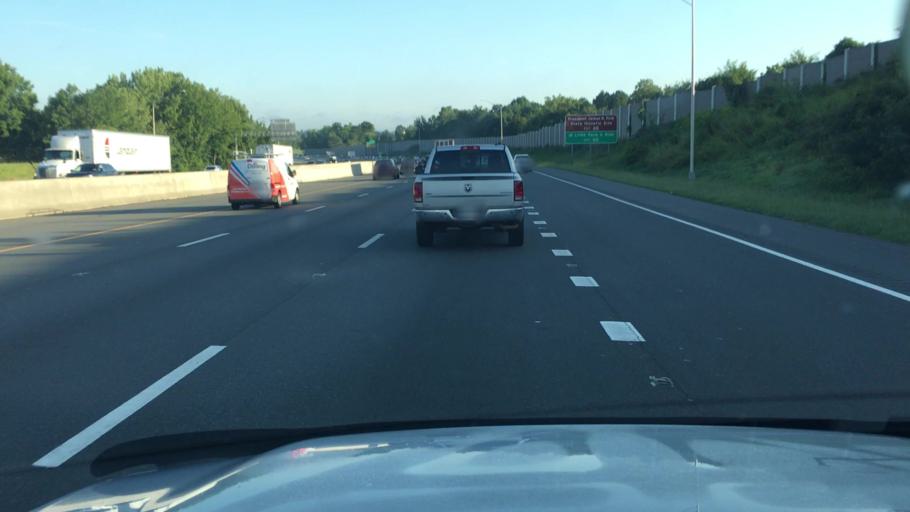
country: US
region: North Carolina
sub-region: Mecklenburg County
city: Pineville
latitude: 35.0943
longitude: -80.8755
